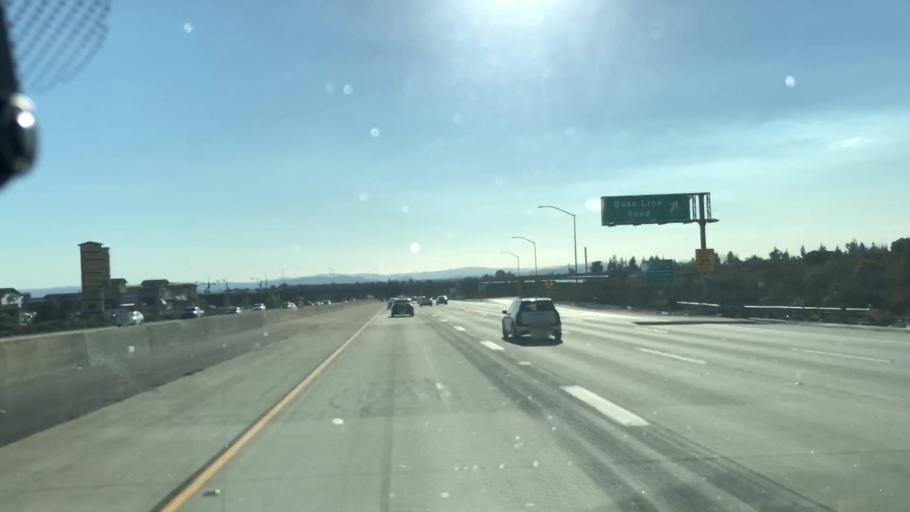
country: US
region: California
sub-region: Los Angeles County
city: Claremont
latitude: 34.1253
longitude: -117.6914
